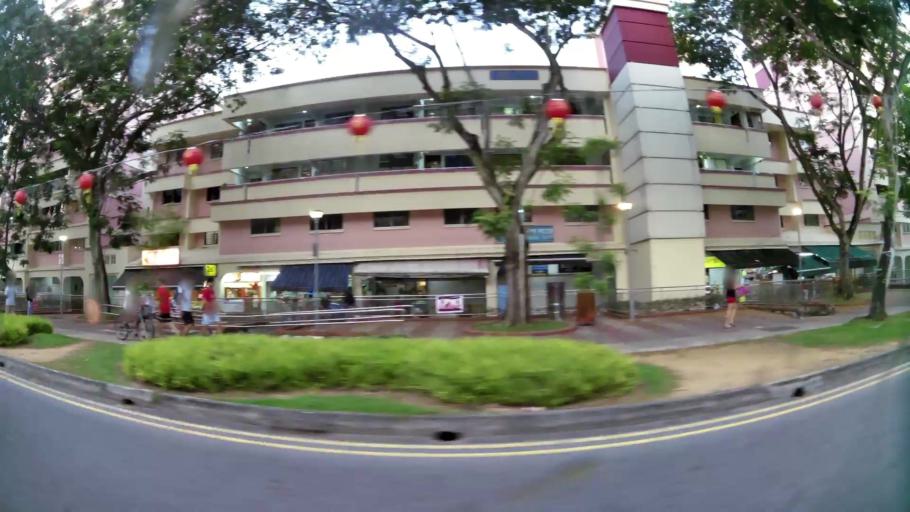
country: MY
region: Johor
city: Kampung Pasir Gudang Baru
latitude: 1.4351
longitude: 103.8385
